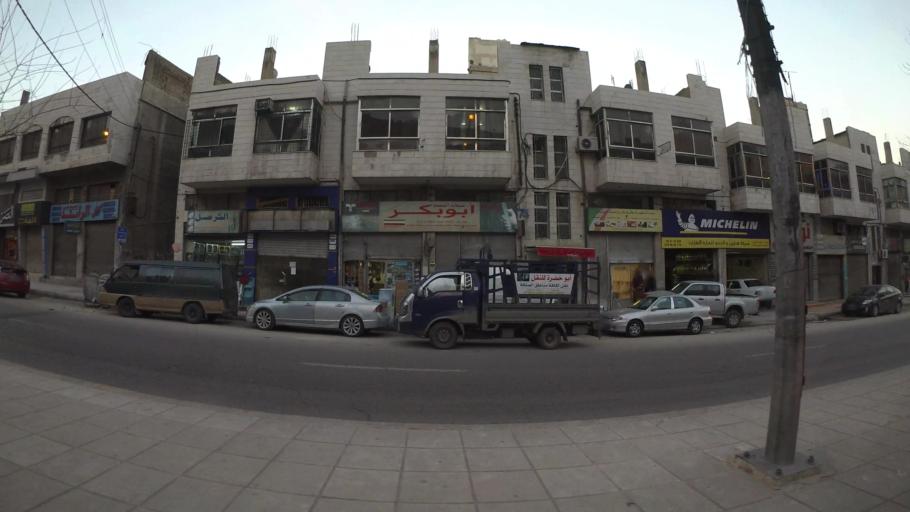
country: JO
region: Amman
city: Amman
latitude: 31.9386
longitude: 35.9238
